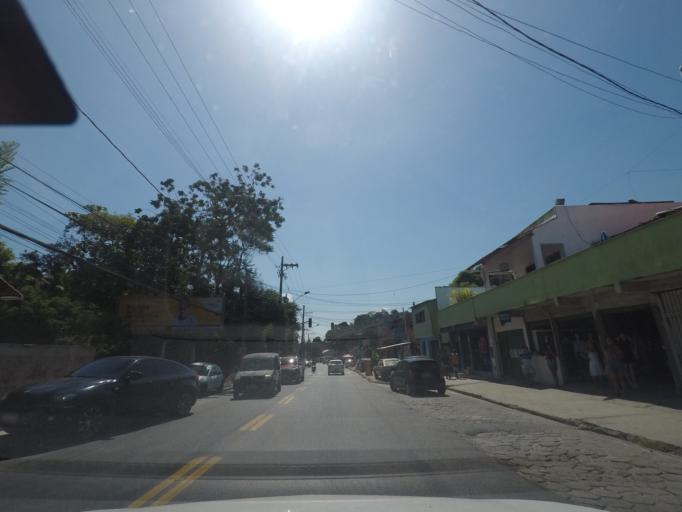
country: BR
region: Rio de Janeiro
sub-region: Niteroi
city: Niteroi
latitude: -22.9104
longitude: -43.0510
